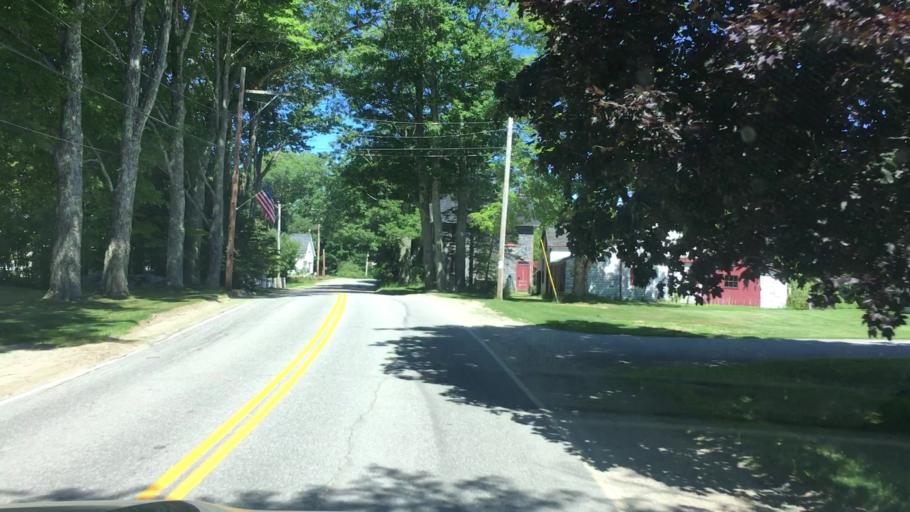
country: US
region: Maine
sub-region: Hancock County
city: Penobscot
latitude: 44.4555
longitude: -68.7028
